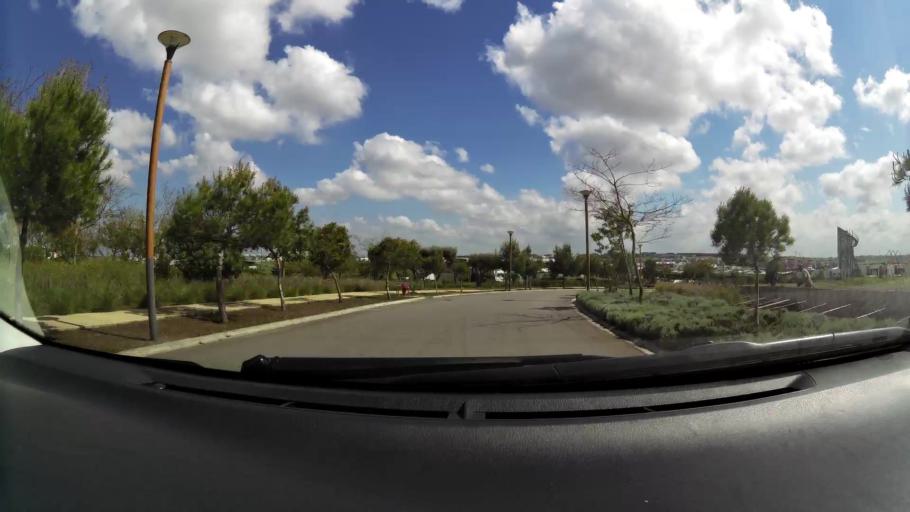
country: MA
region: Grand Casablanca
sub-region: Nouaceur
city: Bouskoura
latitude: 33.4920
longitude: -7.6000
